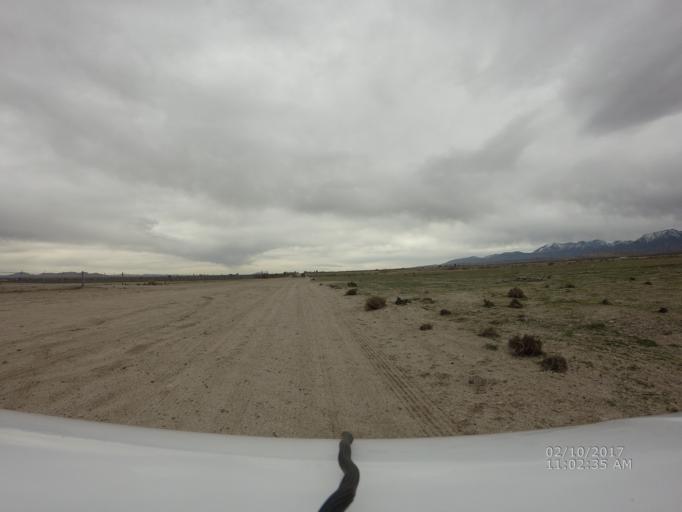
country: US
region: California
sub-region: Los Angeles County
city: Littlerock
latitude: 34.5283
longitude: -117.9511
